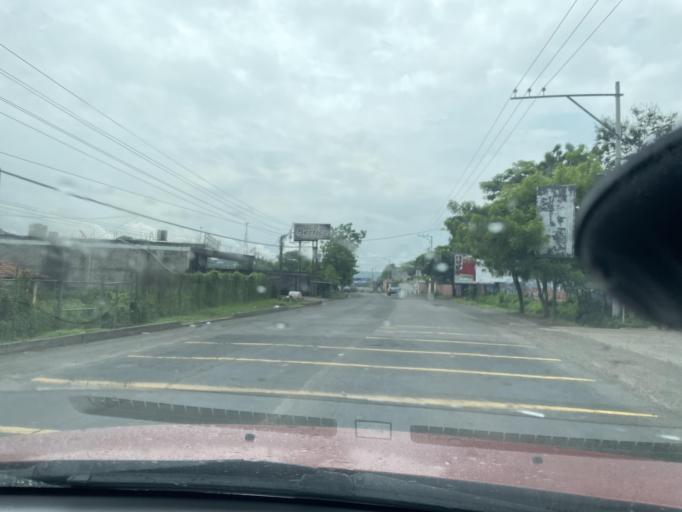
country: SV
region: La Union
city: Santa Rosa de Lima
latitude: 13.6198
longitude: -87.8992
